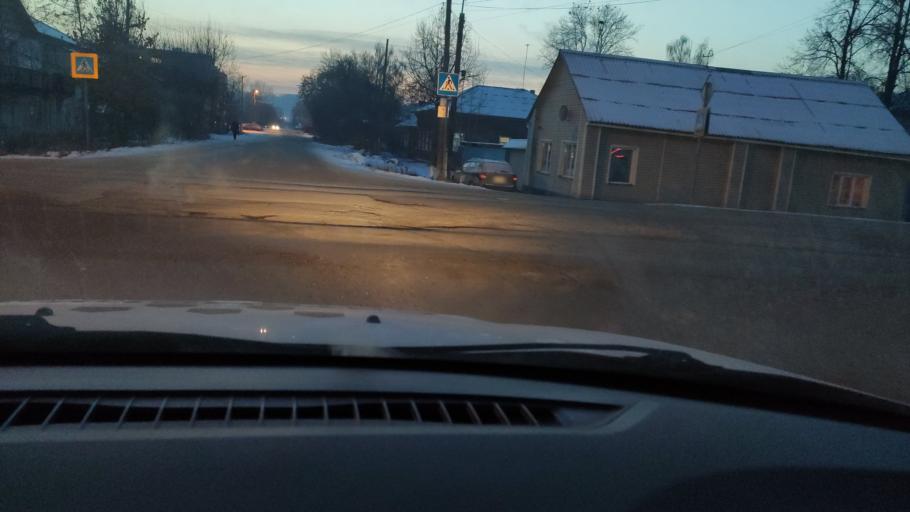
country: RU
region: Perm
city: Kungur
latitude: 57.4357
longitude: 56.9305
